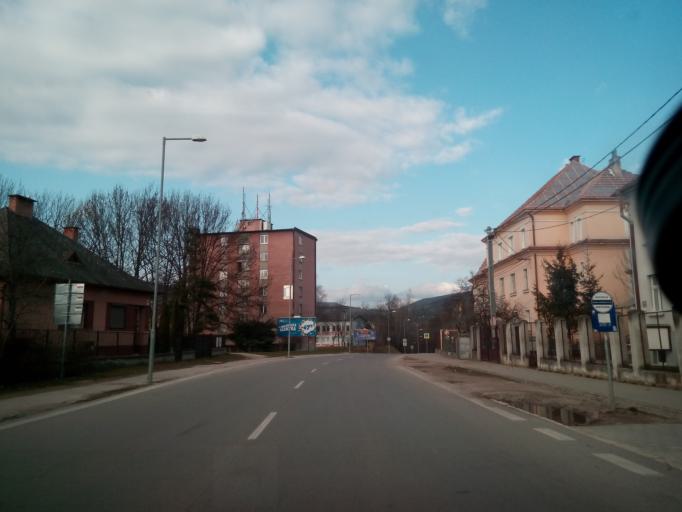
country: SK
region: Kosicky
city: Roznava
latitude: 48.6592
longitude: 20.5286
